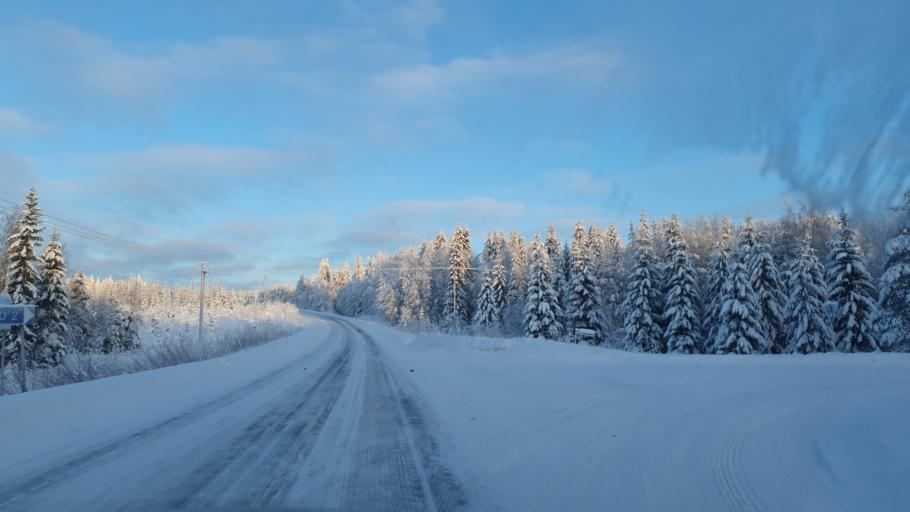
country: FI
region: Kainuu
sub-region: Kajaani
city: Vuokatti
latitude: 64.2144
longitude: 28.2468
